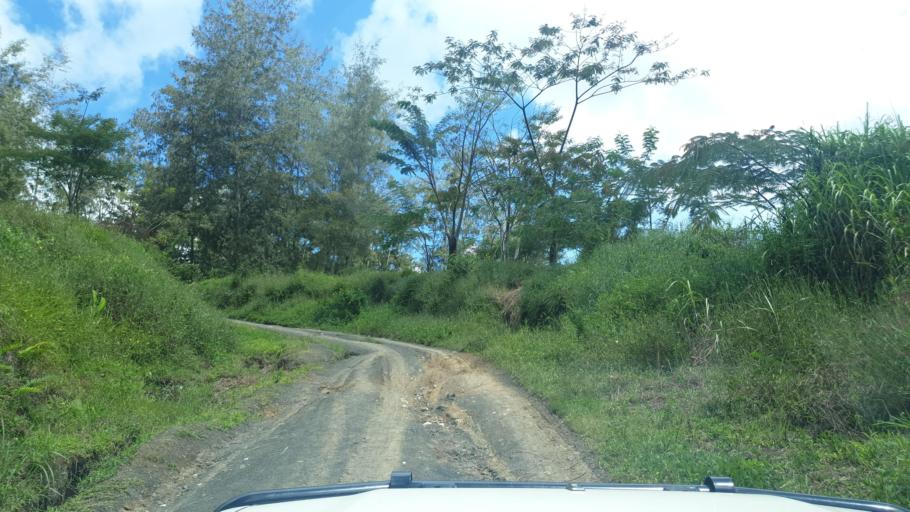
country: PG
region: Chimbu
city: Kundiawa
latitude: -6.2599
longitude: 145.1378
